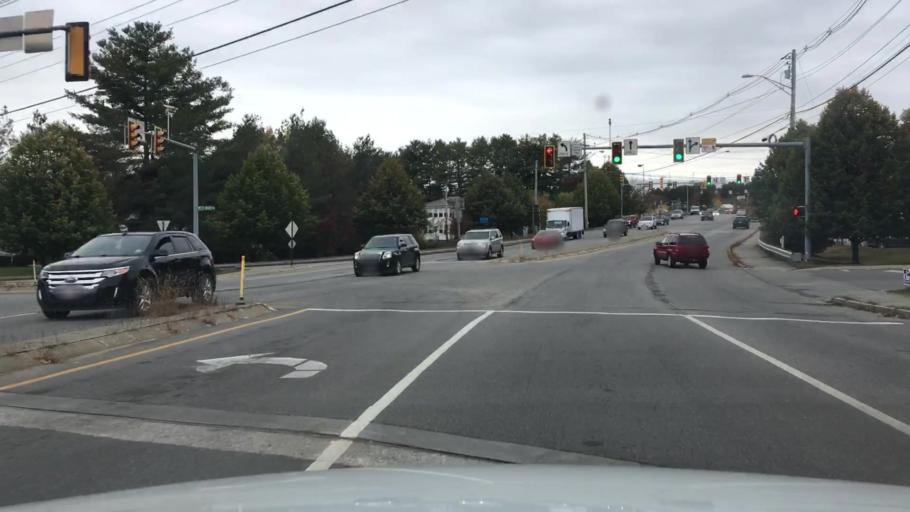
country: US
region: Maine
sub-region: Kennebec County
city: Waterville
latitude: 44.5402
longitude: -69.6490
